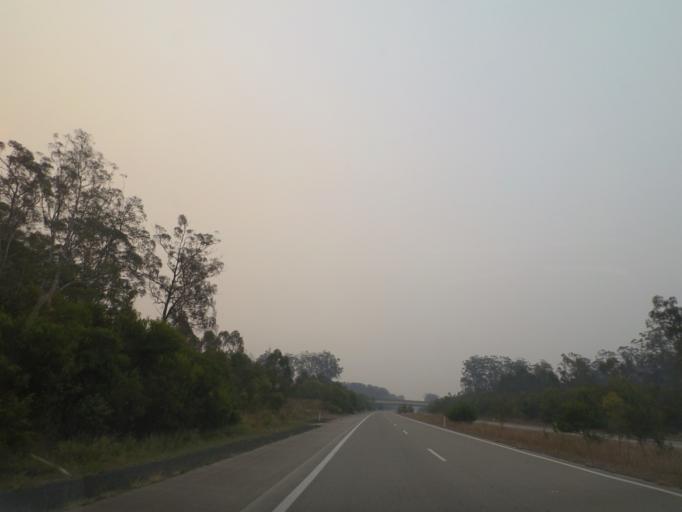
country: AU
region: New South Wales
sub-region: Kempsey
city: Frederickton
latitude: -31.0122
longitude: 152.8669
